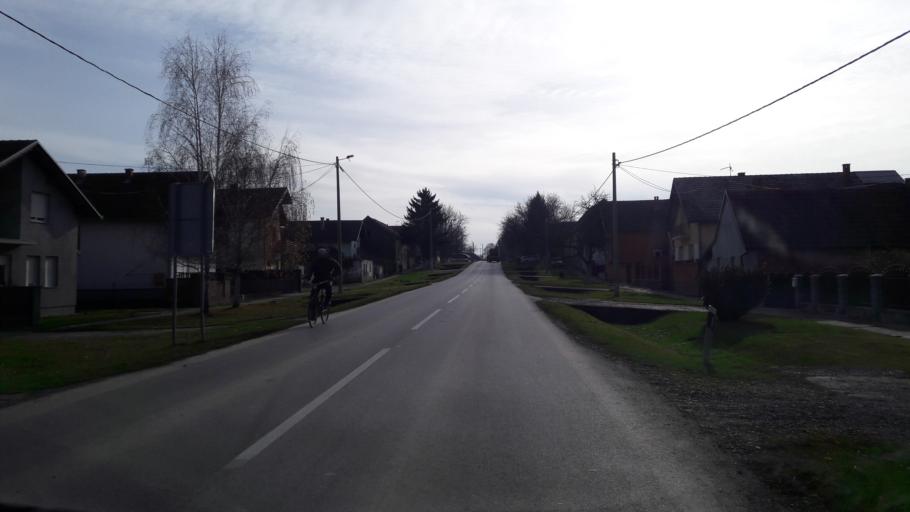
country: HR
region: Osjecko-Baranjska
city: Semeljci
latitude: 45.3556
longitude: 18.5541
